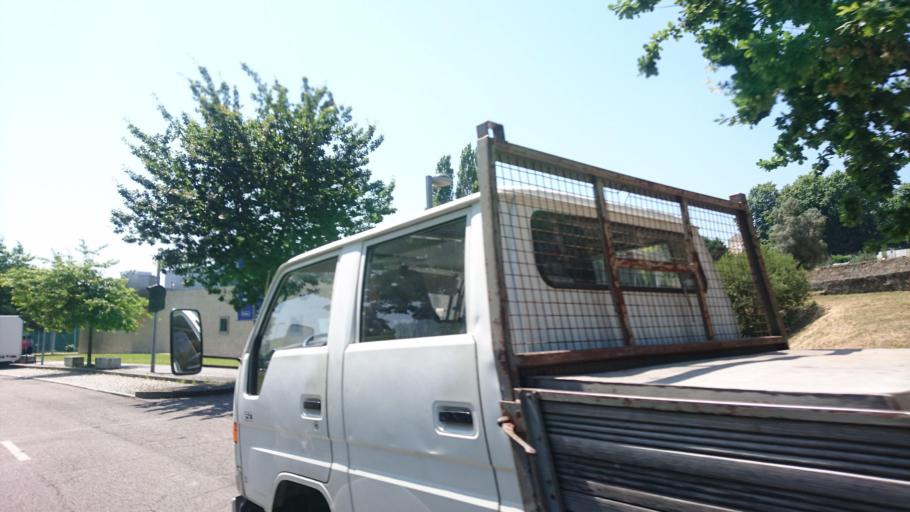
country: PT
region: Porto
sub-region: Gondomar
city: Rio Tinto
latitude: 41.1602
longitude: -8.5735
